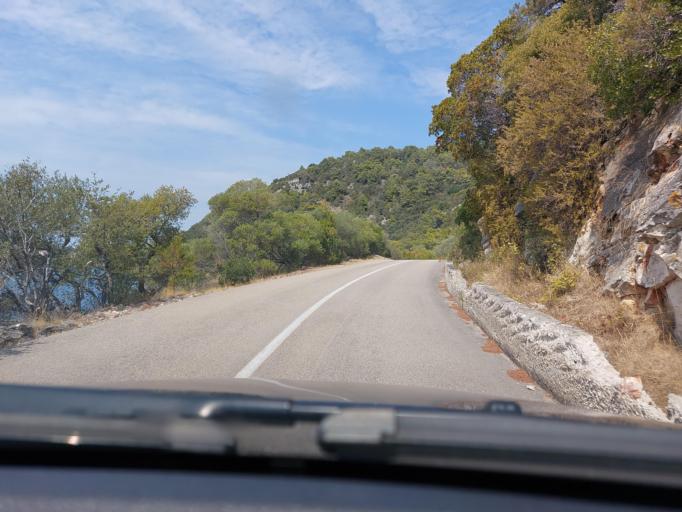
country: HR
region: Dubrovacko-Neretvanska
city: Smokvica
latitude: 42.7584
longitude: 16.8231
